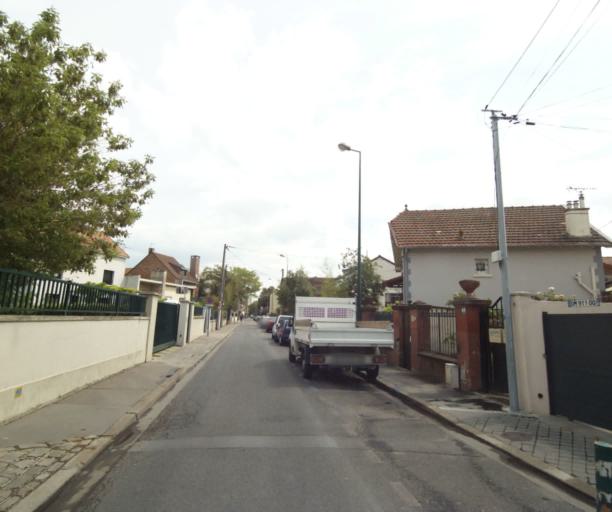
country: FR
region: Ile-de-France
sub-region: Departement des Hauts-de-Seine
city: Colombes
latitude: 48.9304
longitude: 2.2571
